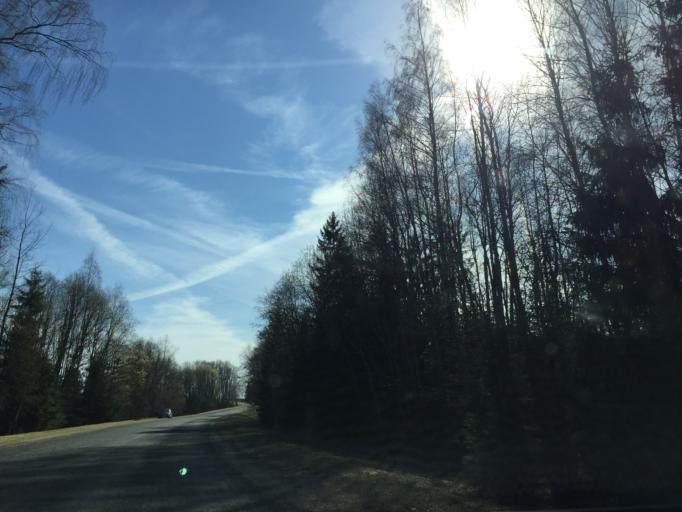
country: EE
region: Vorumaa
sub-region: Antsla vald
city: Vana-Antsla
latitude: 57.9974
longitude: 26.4231
